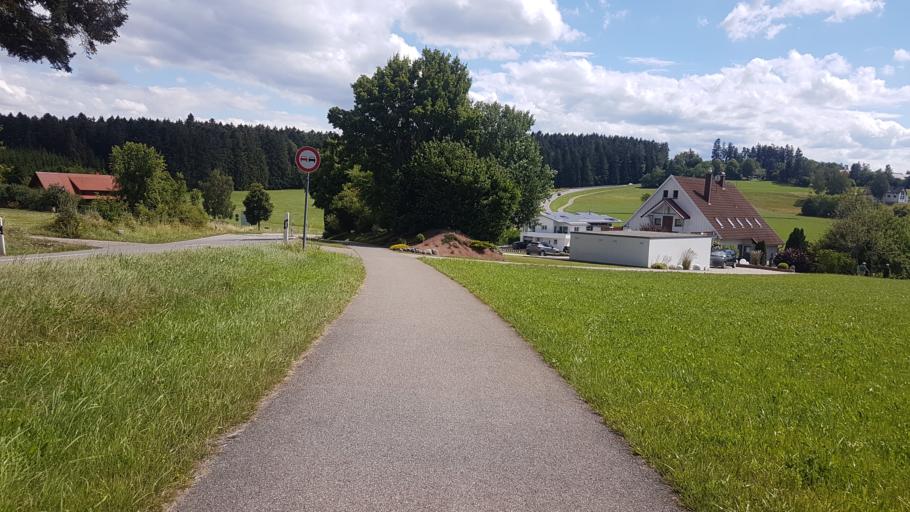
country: DE
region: Baden-Wuerttemberg
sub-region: Freiburg Region
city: Hardt
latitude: 48.1963
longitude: 8.4129
